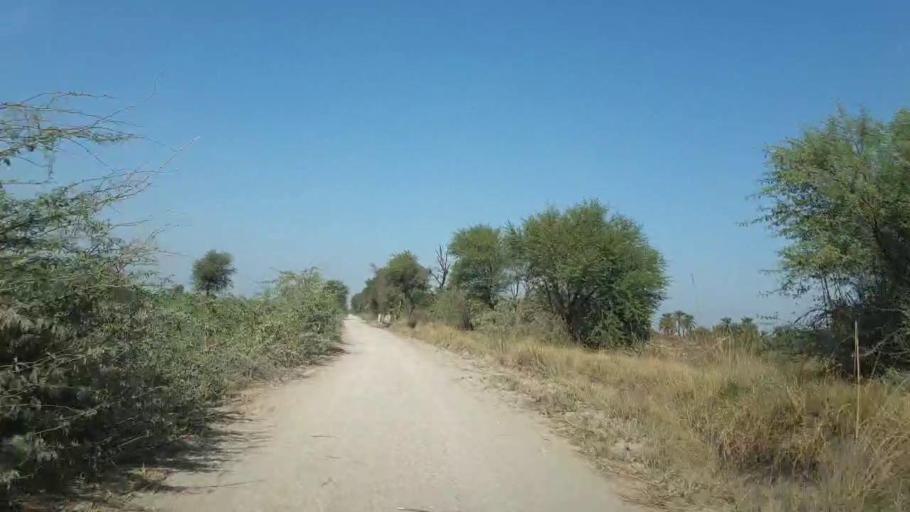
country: PK
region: Sindh
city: Mirpur Khas
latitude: 25.6492
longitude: 69.0275
